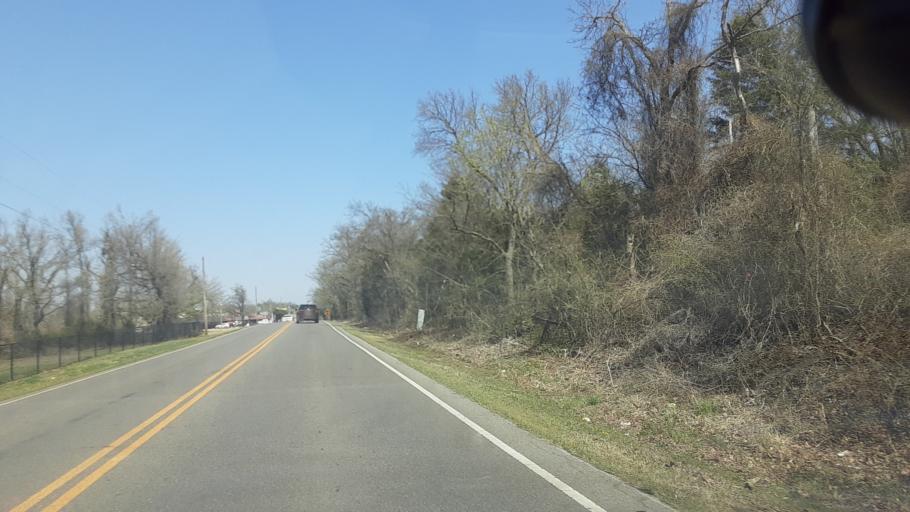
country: US
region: Oklahoma
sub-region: Oklahoma County
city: Edmond
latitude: 35.7222
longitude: -97.4783
